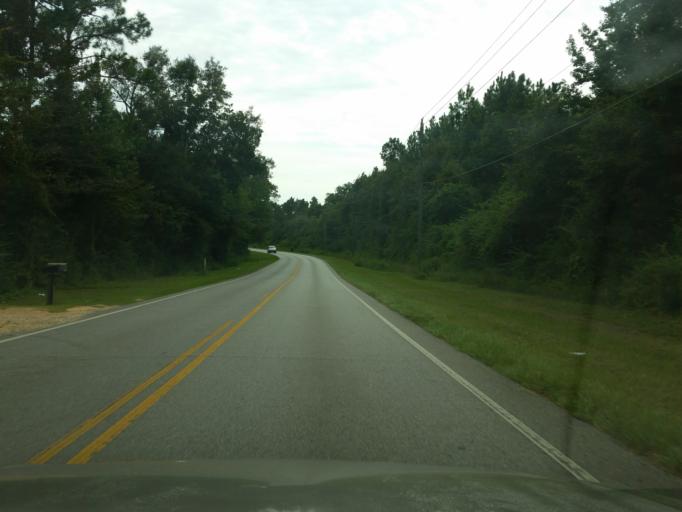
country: US
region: Florida
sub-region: Escambia County
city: Molino
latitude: 30.6653
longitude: -87.3213
